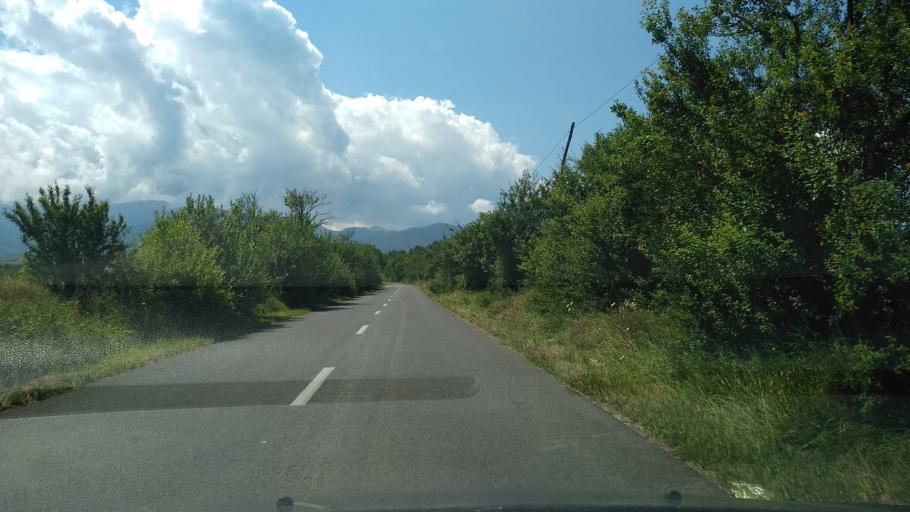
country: RO
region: Hunedoara
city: Salasu de Sus
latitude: 45.5176
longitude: 22.9592
